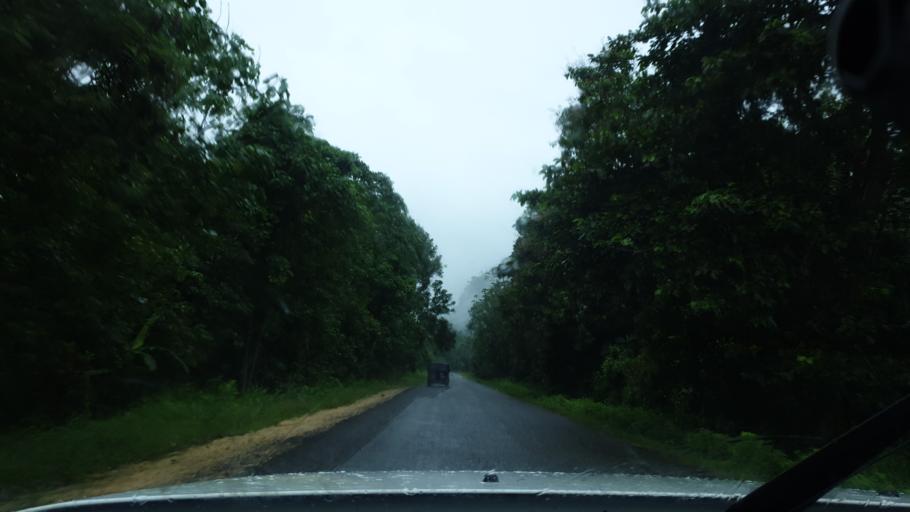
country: PG
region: Madang
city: Madang
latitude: -5.3086
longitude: 145.7248
